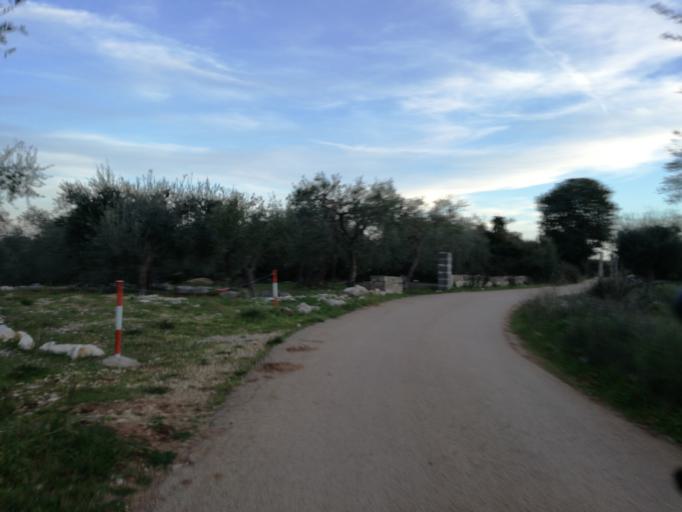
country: IT
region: Apulia
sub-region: Provincia di Bari
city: Lamie
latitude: 41.0232
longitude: 16.8718
